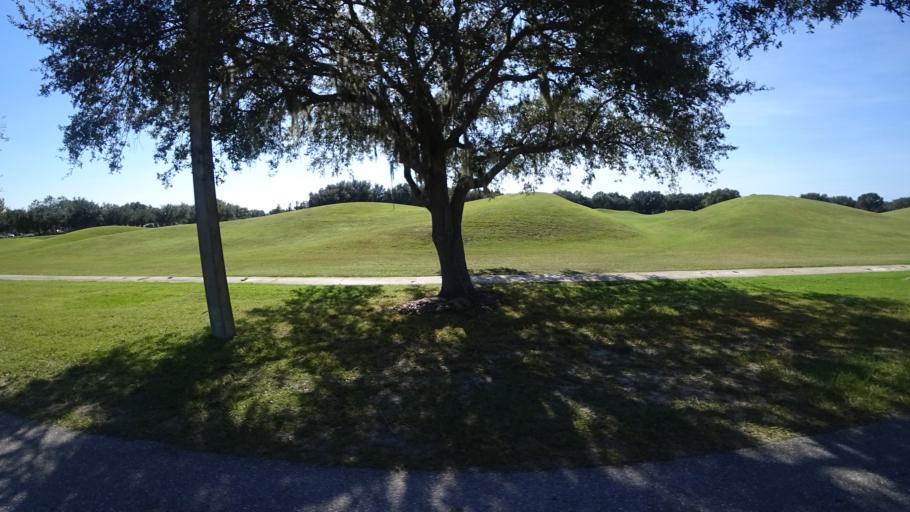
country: US
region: Florida
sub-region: Sarasota County
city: The Meadows
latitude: 27.4256
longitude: -82.4345
